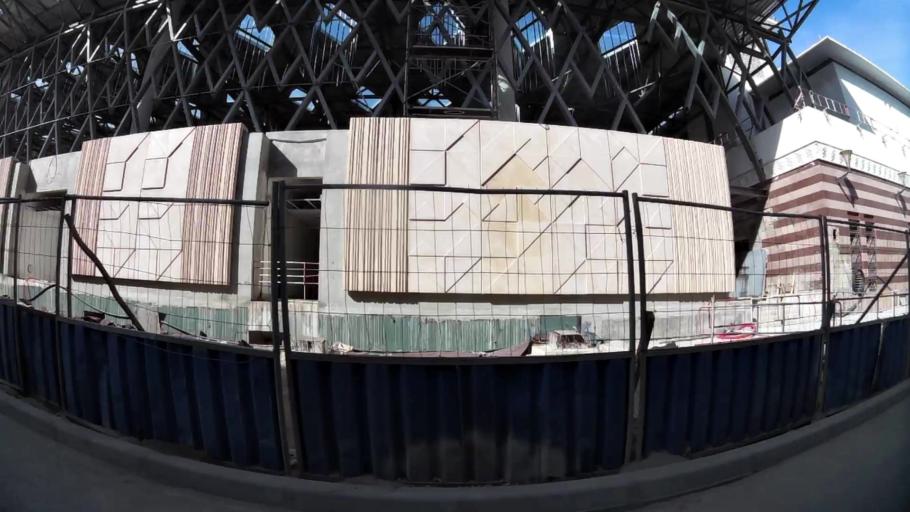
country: MA
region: Tanger-Tetouan
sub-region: Tanger-Assilah
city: Tangier
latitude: 35.7714
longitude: -5.7854
